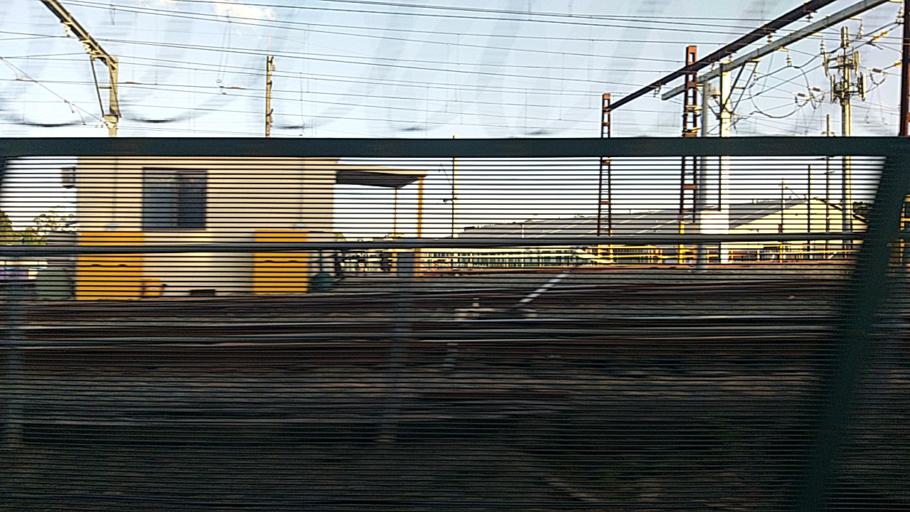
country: AU
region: New South Wales
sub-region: Hurstville
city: Penshurst
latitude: -33.9739
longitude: 151.0798
